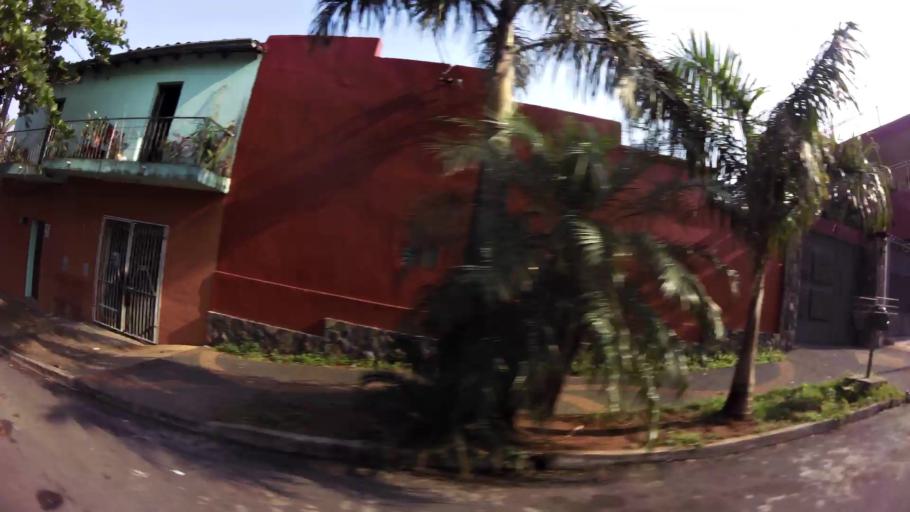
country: PY
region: Presidente Hayes
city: Nanawa
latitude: -25.2796
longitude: -57.6576
